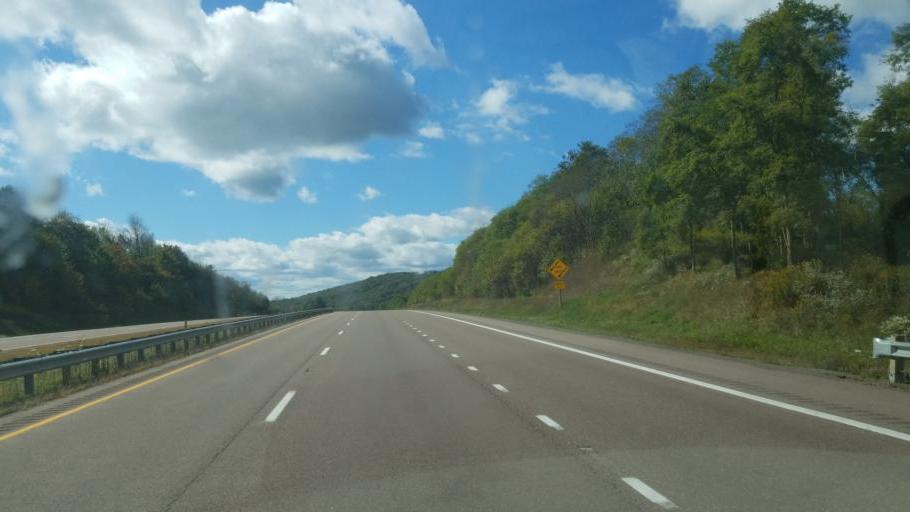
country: US
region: Pennsylvania
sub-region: Somerset County
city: Meyersdale
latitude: 39.7009
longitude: -79.2967
